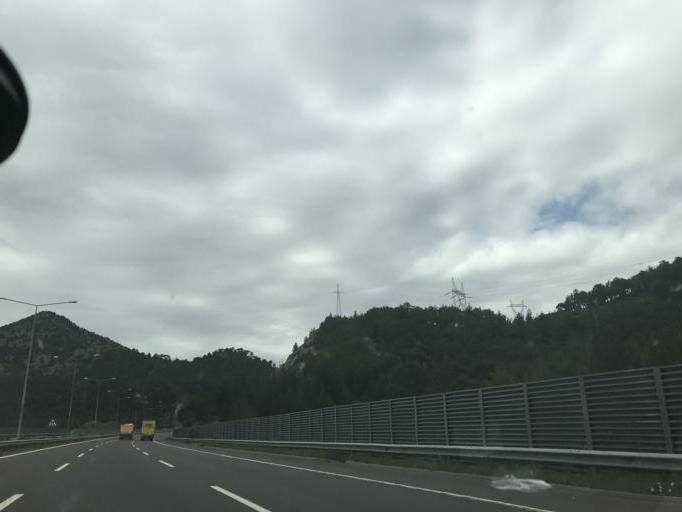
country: TR
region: Nigde
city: Ciftehan
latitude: 37.5028
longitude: 34.8234
